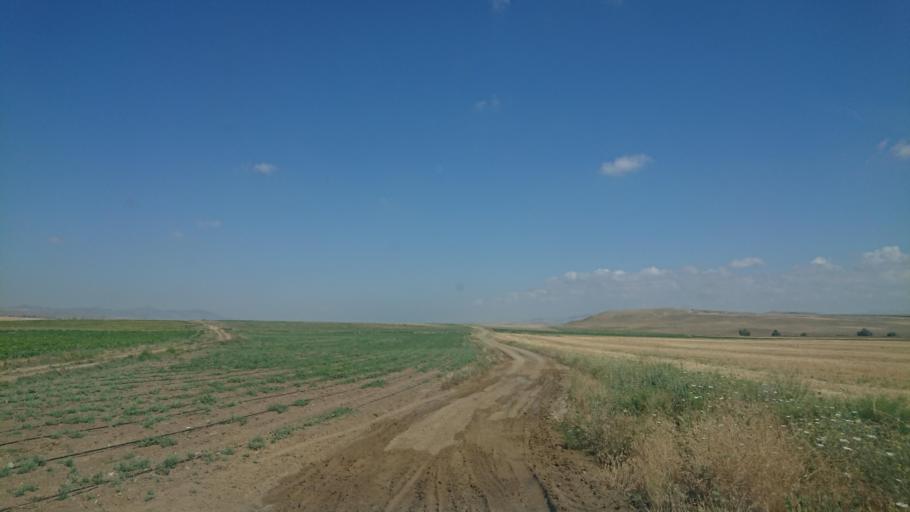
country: TR
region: Aksaray
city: Sariyahsi
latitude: 38.9636
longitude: 33.9265
